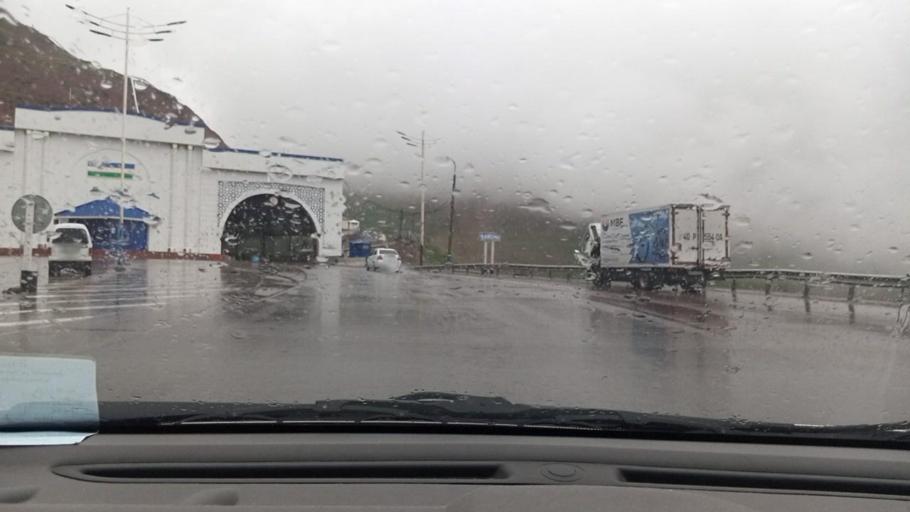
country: UZ
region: Toshkent
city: Angren
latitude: 41.1033
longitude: 70.5138
